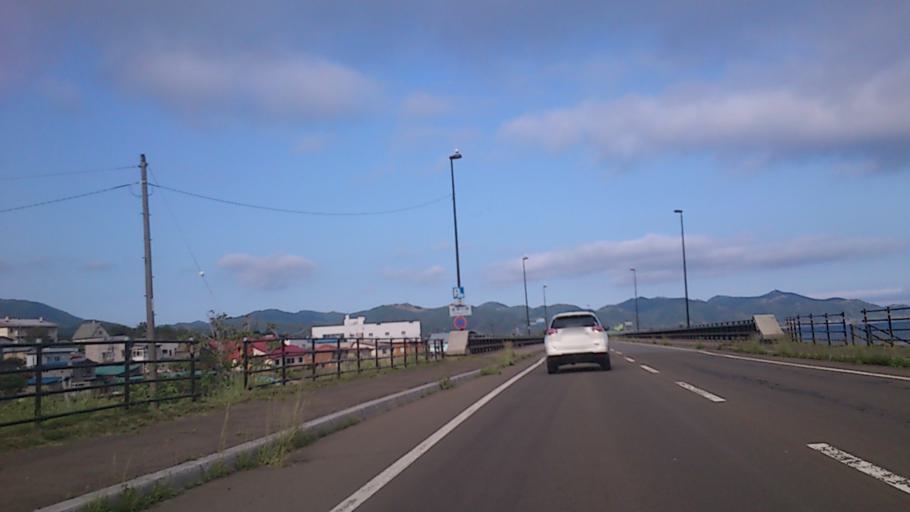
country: JP
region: Aomori
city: Shimokizukuri
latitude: 41.4260
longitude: 140.1017
